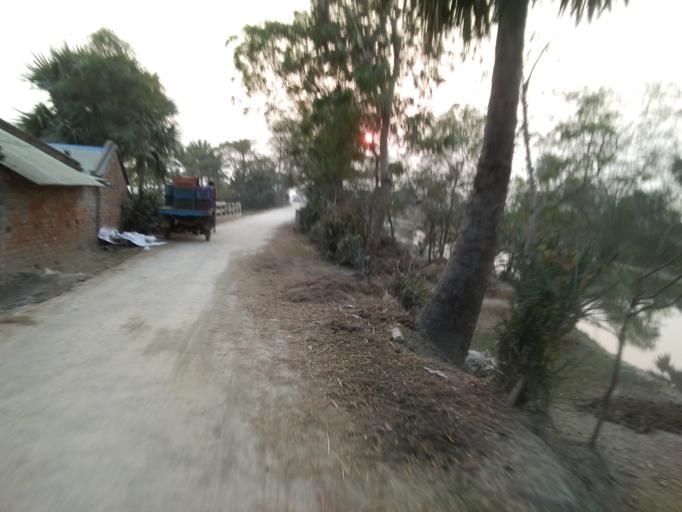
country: BD
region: Khulna
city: Satkhira
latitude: 22.6538
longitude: 89.0219
